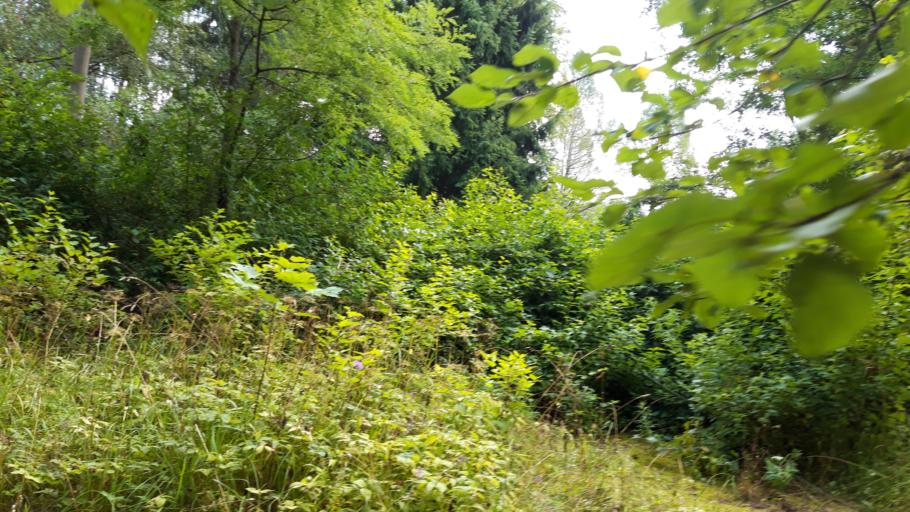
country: RU
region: Tverskaya
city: Konakovo
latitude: 56.6680
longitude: 36.6830
